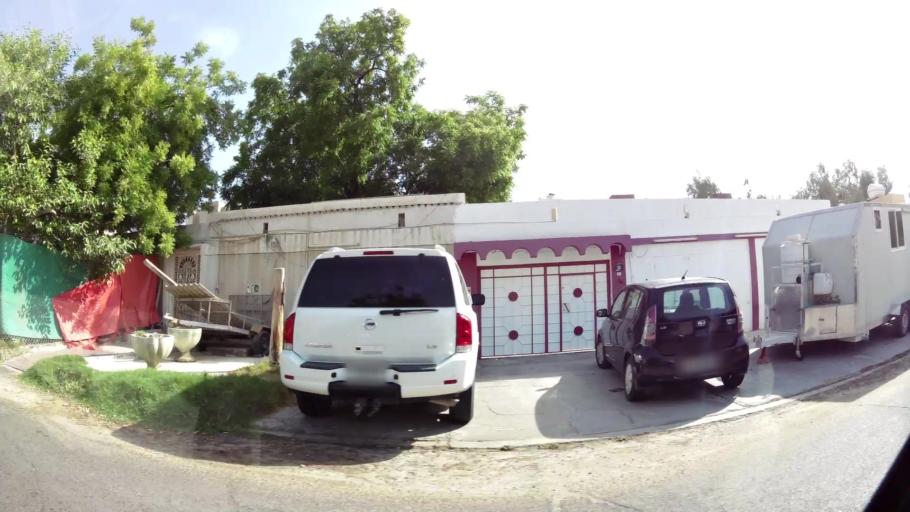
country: AE
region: Ash Shariqah
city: Sharjah
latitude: 25.2215
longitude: 55.3912
